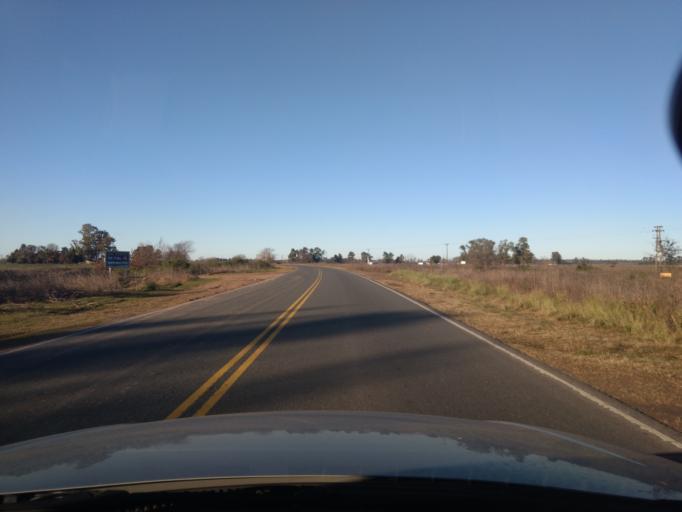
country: AR
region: Buenos Aires
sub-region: Partido de Lujan
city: Lujan
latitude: -34.6288
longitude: -59.1089
